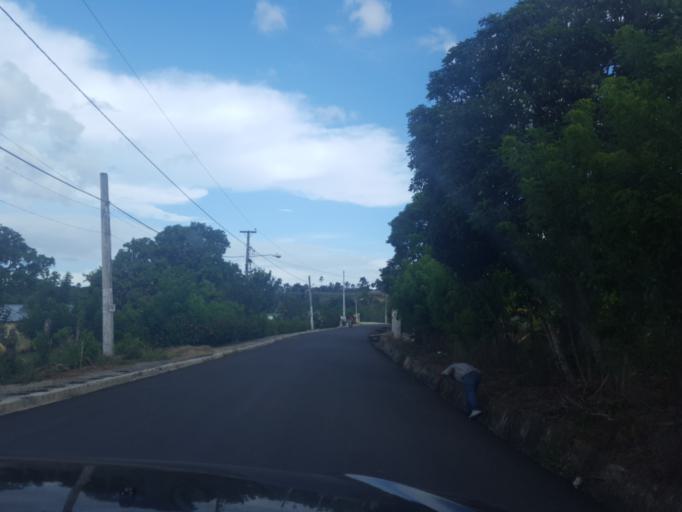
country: DO
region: Santiago
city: Baitoa
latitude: 19.3584
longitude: -70.6335
